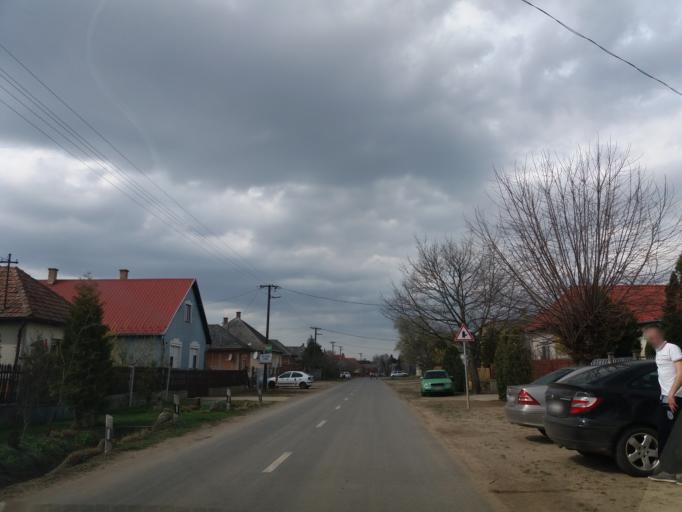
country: HU
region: Szabolcs-Szatmar-Bereg
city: Nyirtass
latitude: 48.1057
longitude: 22.0272
